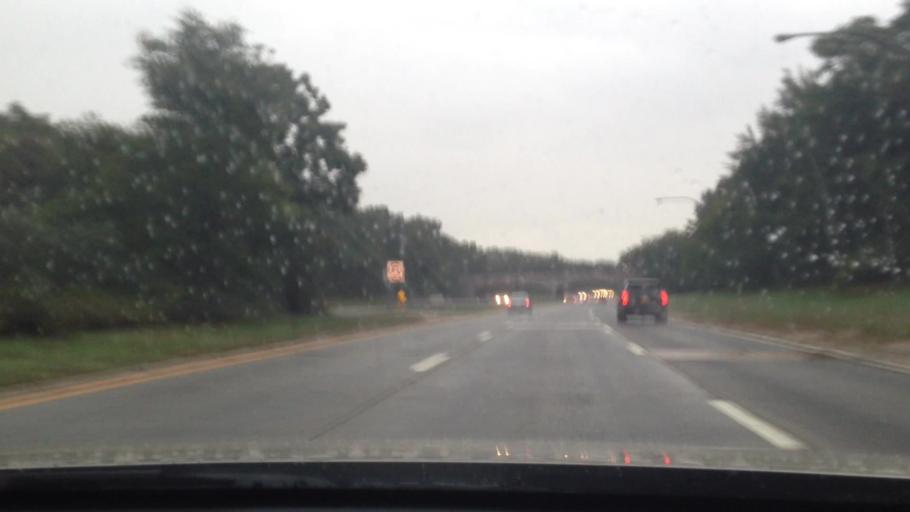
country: US
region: New York
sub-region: Suffolk County
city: North Bay Shore
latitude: 40.7511
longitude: -73.2456
